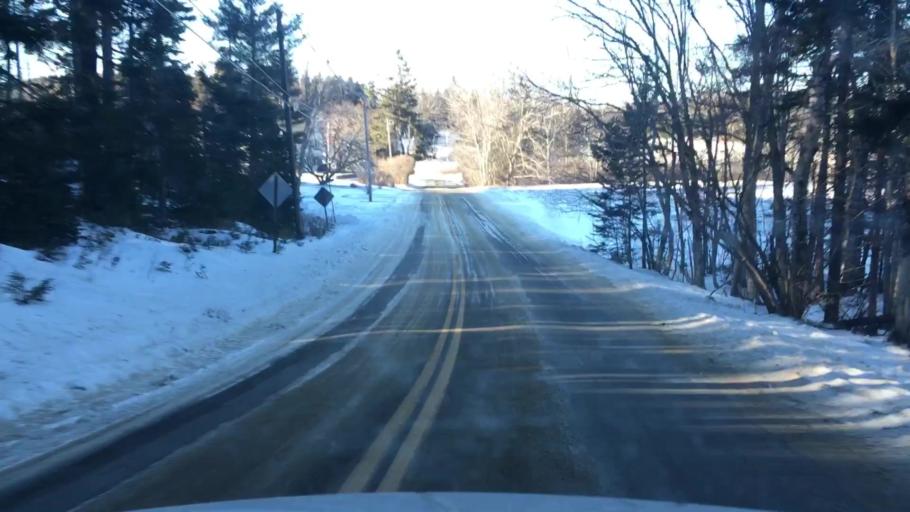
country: US
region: Maine
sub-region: Hancock County
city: Castine
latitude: 44.3460
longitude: -68.7461
